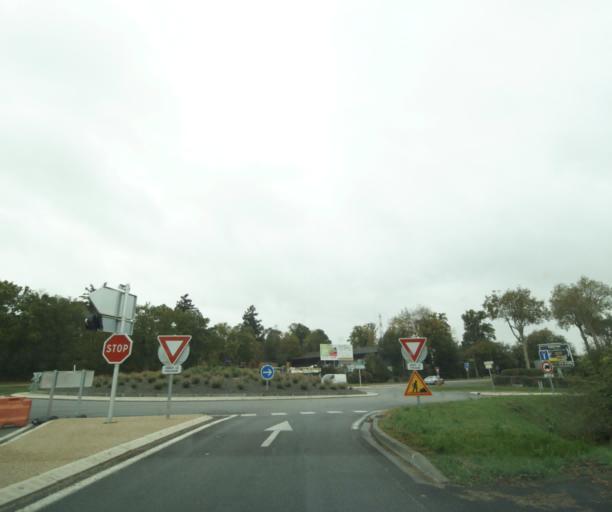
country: FR
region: Centre
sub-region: Departement d'Eure-et-Loir
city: Luray
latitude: 48.7444
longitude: 1.3918
